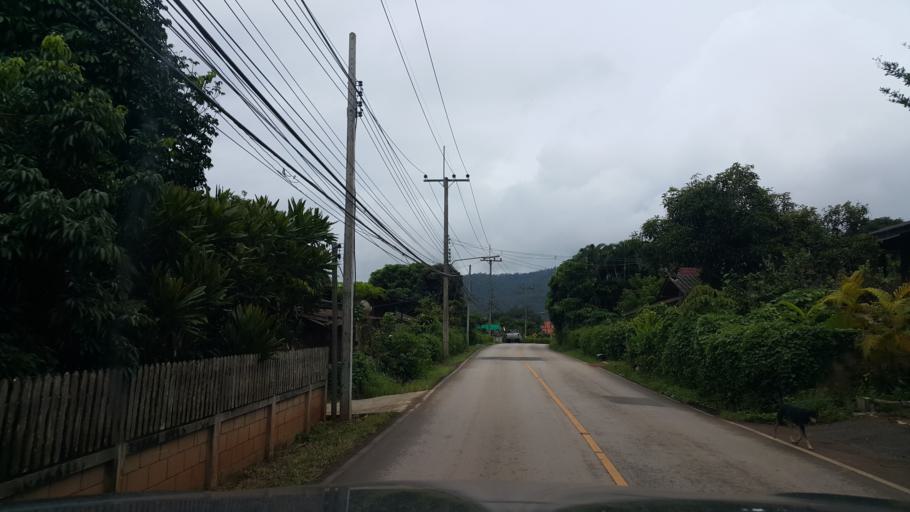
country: TH
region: Chiang Mai
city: Samoeng
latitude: 18.8593
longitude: 98.7020
